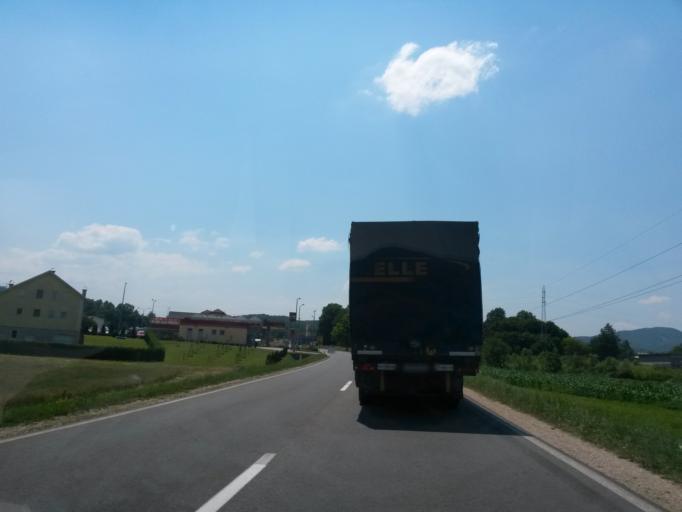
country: BA
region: Federation of Bosnia and Herzegovina
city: Lijesnica
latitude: 44.4826
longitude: 18.0694
